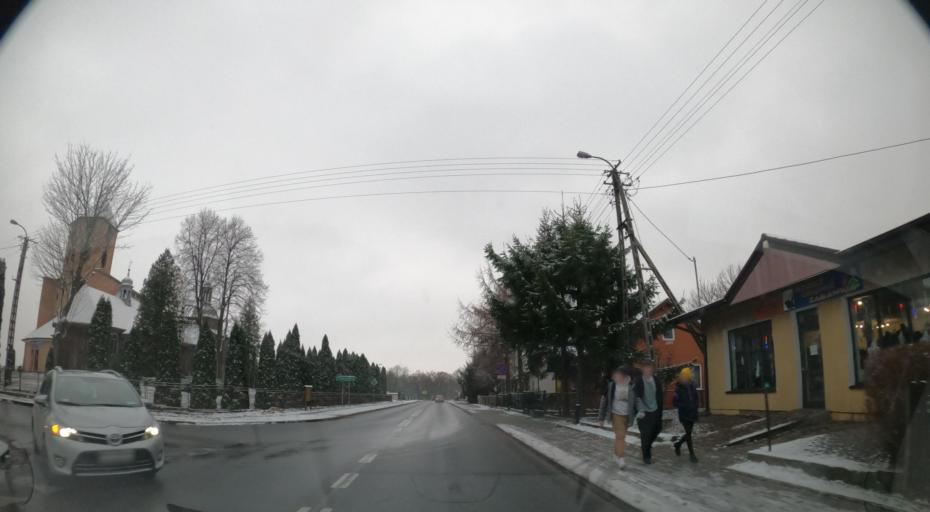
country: PL
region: Kujawsko-Pomorskie
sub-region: Powiat lipnowski
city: Wielgie
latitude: 52.7409
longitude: 19.2634
